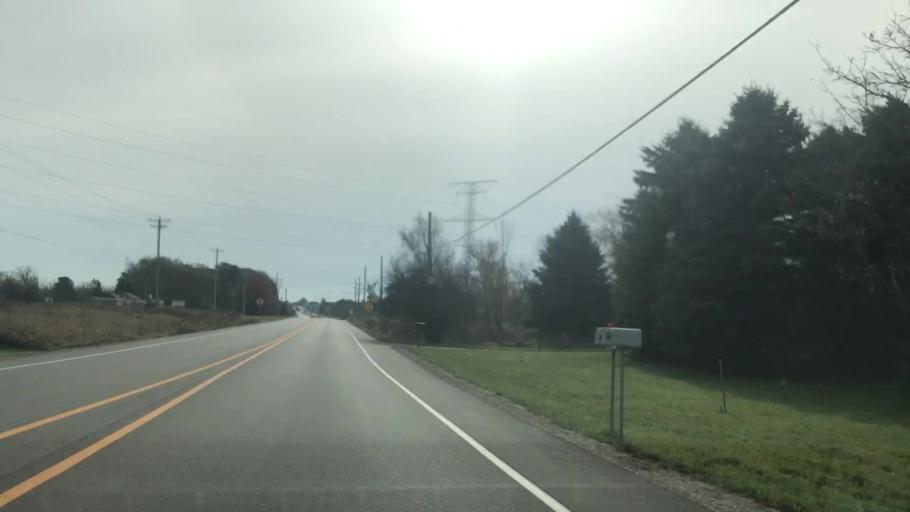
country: US
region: Wisconsin
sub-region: Waukesha County
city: Menomonee Falls
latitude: 43.2011
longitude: -88.1499
